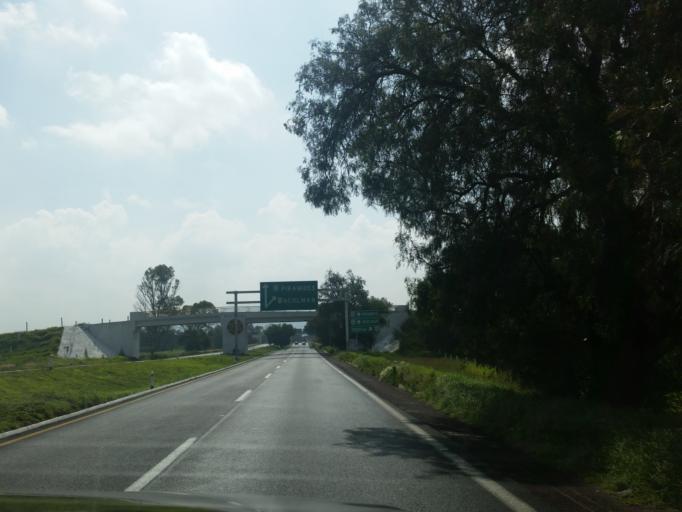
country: MX
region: Mexico
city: Acolman
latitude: 19.6285
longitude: -98.9218
